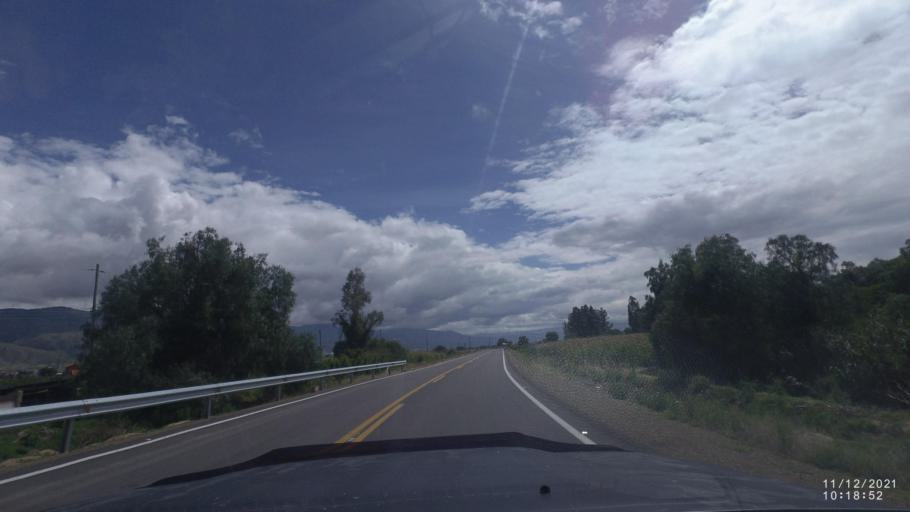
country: BO
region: Cochabamba
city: Tarata
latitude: -17.5756
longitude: -66.0126
